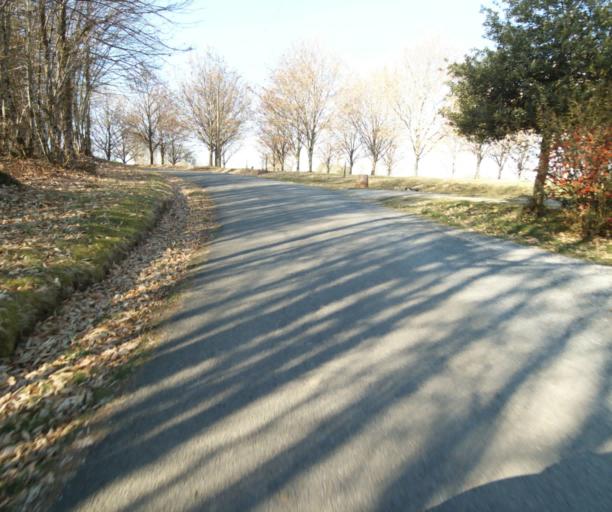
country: FR
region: Limousin
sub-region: Departement de la Correze
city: Saint-Clement
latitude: 45.3710
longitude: 1.6492
